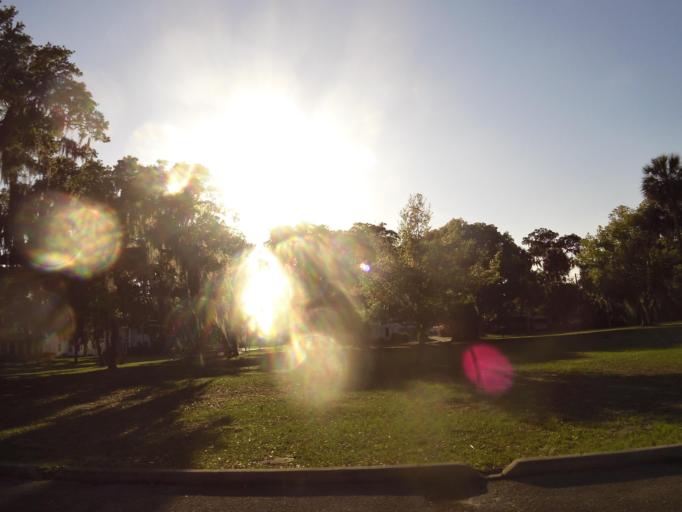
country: US
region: Florida
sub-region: Putnam County
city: Palatka
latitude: 29.6498
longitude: -81.6283
